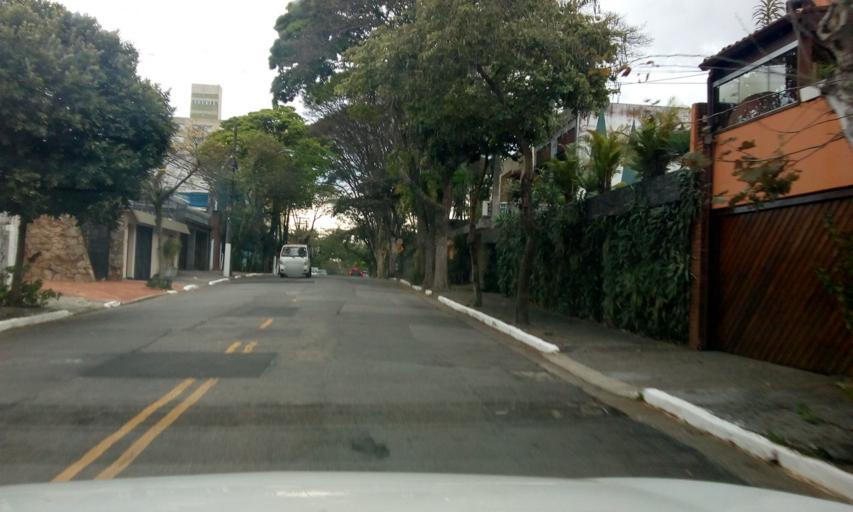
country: BR
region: Sao Paulo
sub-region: Diadema
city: Diadema
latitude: -23.6208
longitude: -46.6486
